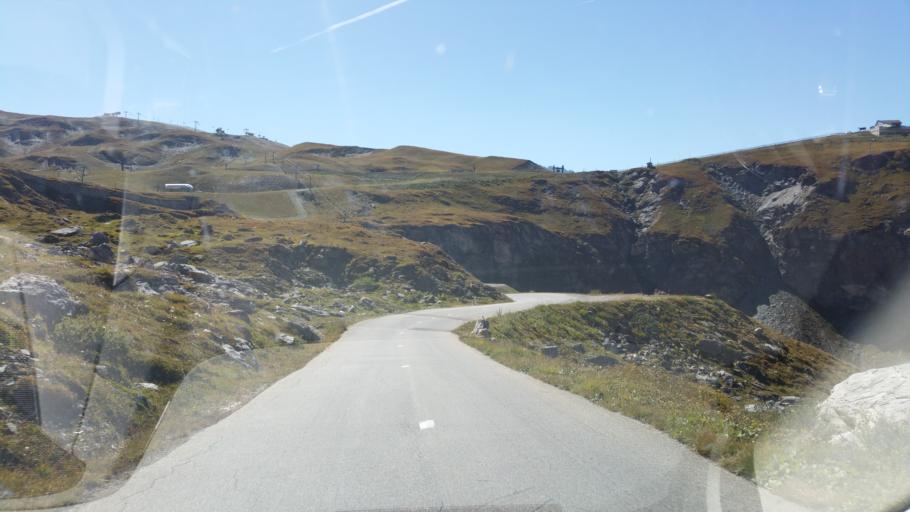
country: FR
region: Rhone-Alpes
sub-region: Departement de la Savoie
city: Val-d'Isere
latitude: 45.4341
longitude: 7.0043
